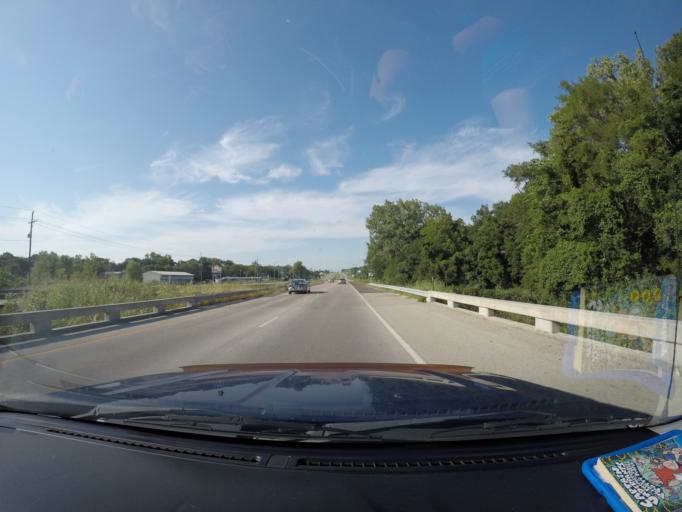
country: US
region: Kansas
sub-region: Leavenworth County
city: Lansing
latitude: 39.2290
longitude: -94.9000
